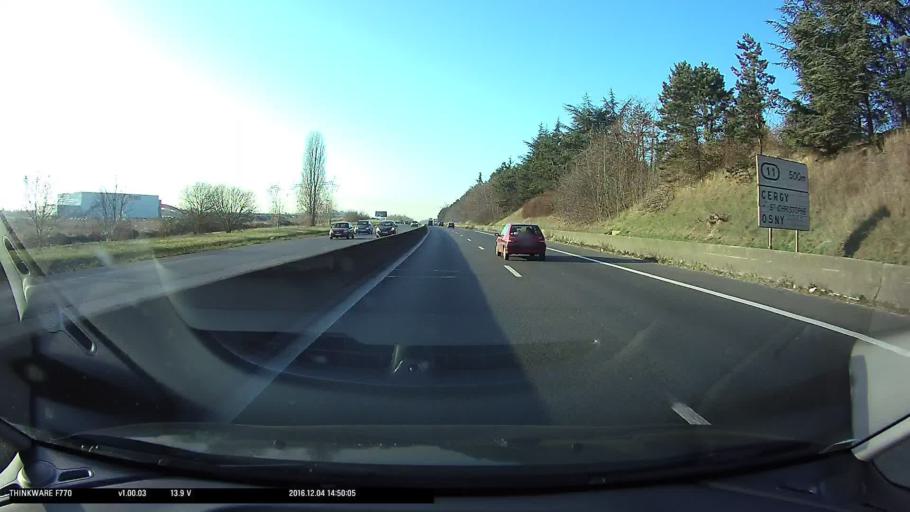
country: FR
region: Ile-de-France
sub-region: Departement du Val-d'Oise
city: Osny
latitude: 49.0542
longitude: 2.0582
